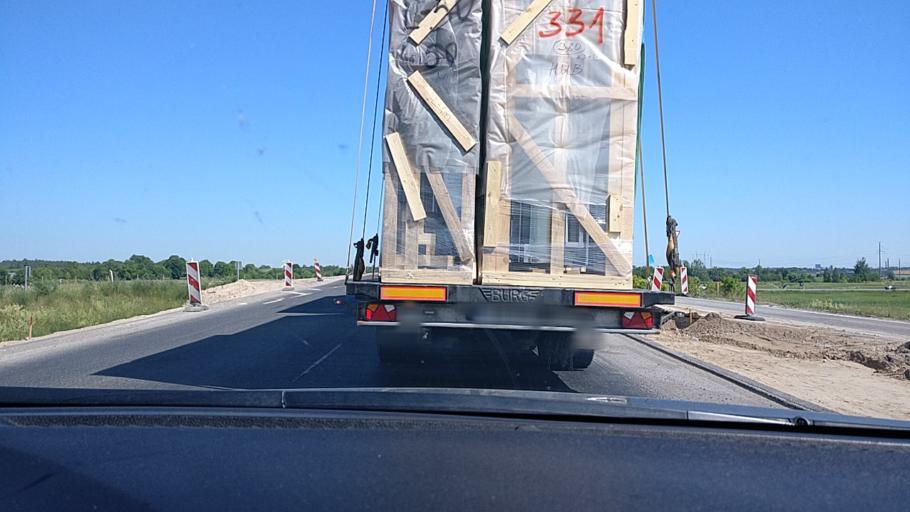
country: LT
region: Panevezys
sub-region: Panevezys City
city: Panevezys
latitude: 55.7333
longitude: 24.2747
